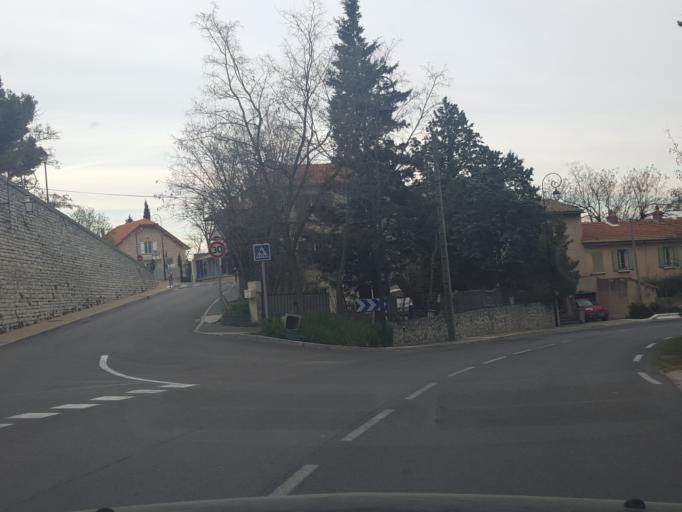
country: FR
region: Provence-Alpes-Cote d'Azur
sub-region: Departement du Vaucluse
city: Chateauneuf-de-Gadagne
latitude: 43.9284
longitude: 4.9459
